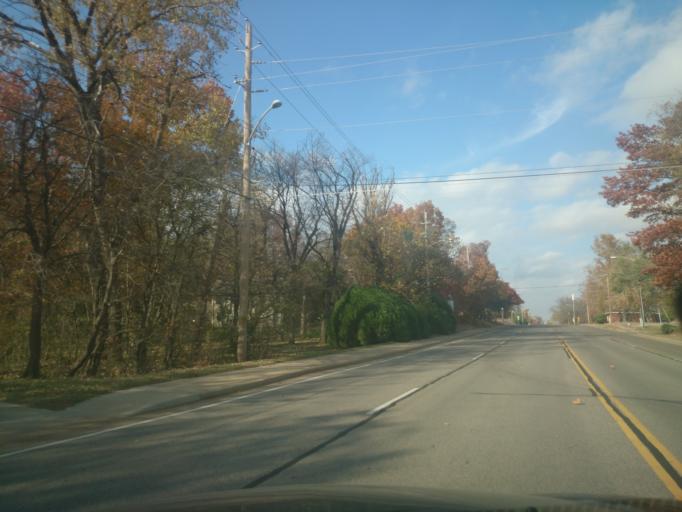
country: US
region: Oklahoma
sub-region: Payne County
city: Stillwater
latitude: 36.1358
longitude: -97.0695
